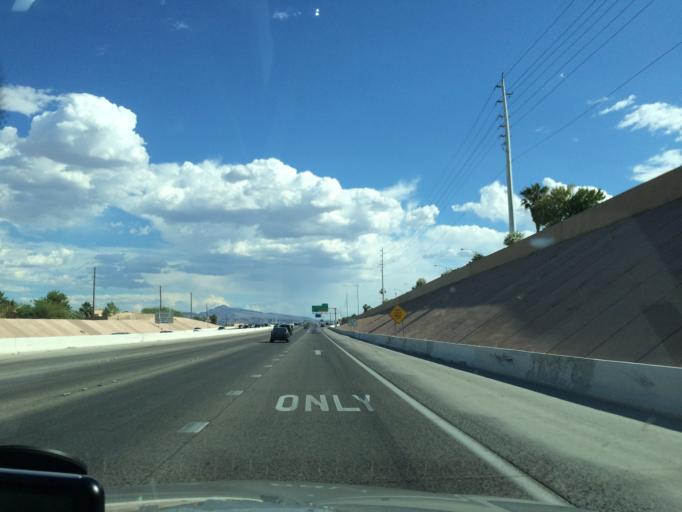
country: US
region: Nevada
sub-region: Clark County
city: Whitney
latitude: 36.1080
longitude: -115.0826
